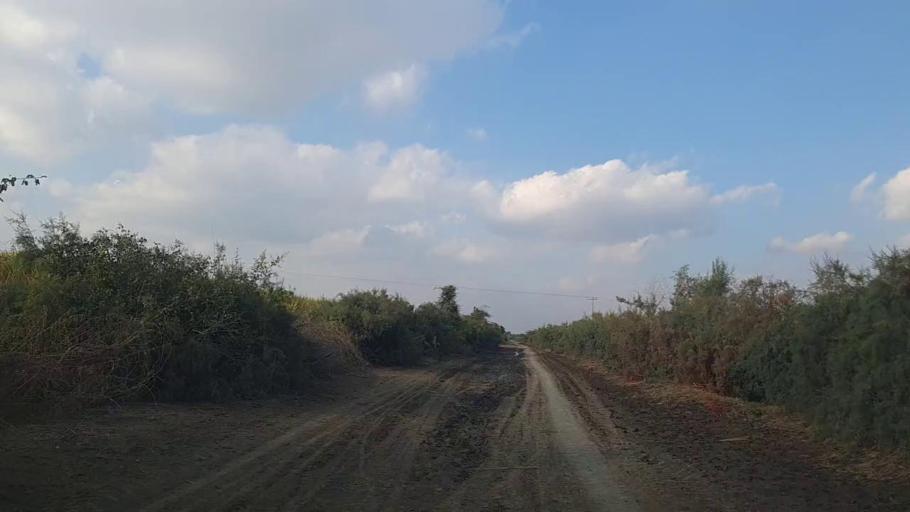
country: PK
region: Sindh
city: Tando Mittha Khan
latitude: 25.9381
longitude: 69.2510
